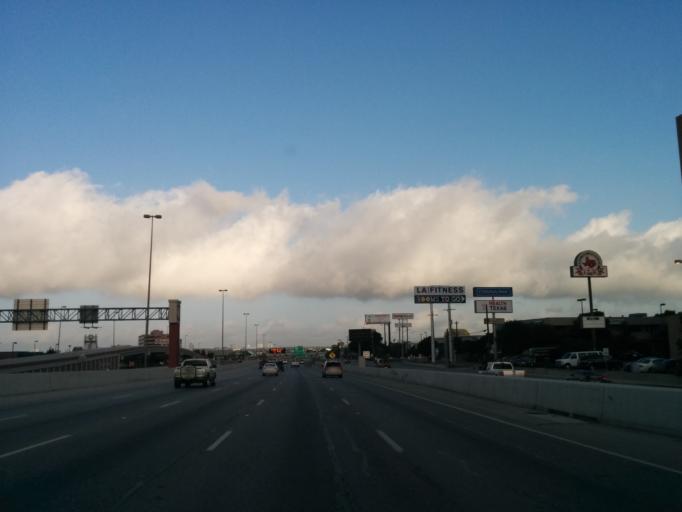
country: US
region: Texas
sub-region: Bexar County
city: Castle Hills
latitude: 29.5207
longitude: -98.5013
